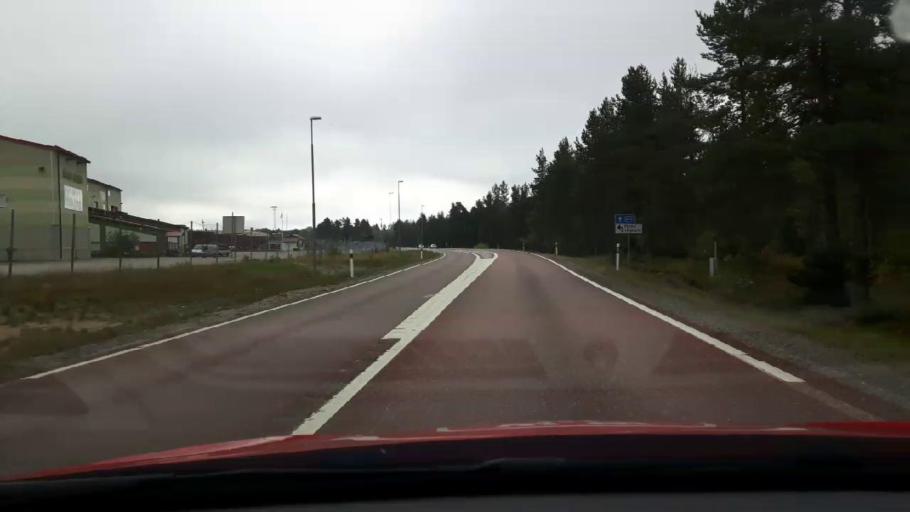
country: SE
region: Gaevleborg
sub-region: Ljusdals Kommun
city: Farila
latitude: 61.8044
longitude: 15.7820
